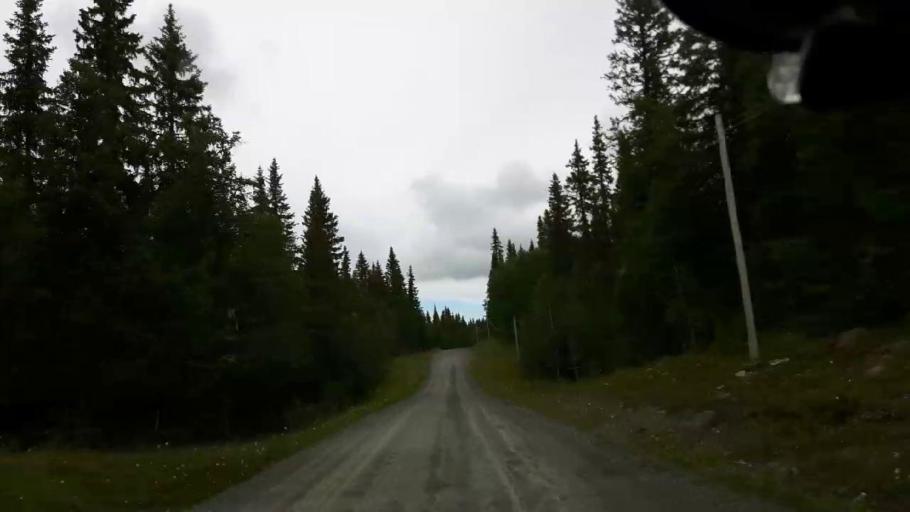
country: SE
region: Jaemtland
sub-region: Krokoms Kommun
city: Valla
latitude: 63.7453
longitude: 13.8359
